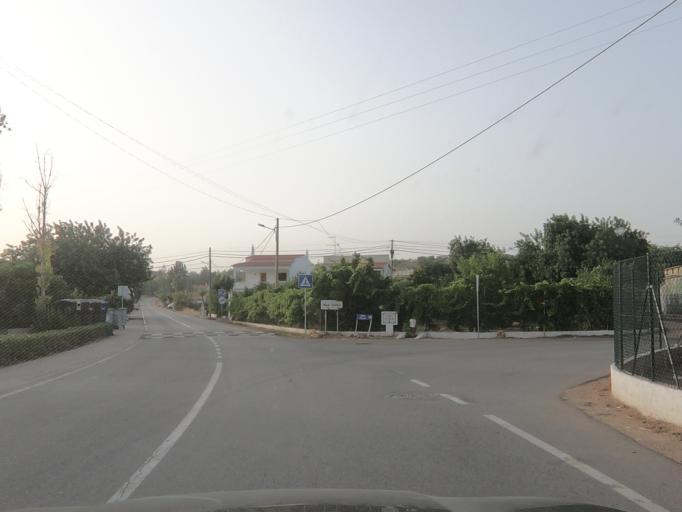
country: PT
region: Faro
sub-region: Loule
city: Vilamoura
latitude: 37.1114
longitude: -8.0886
